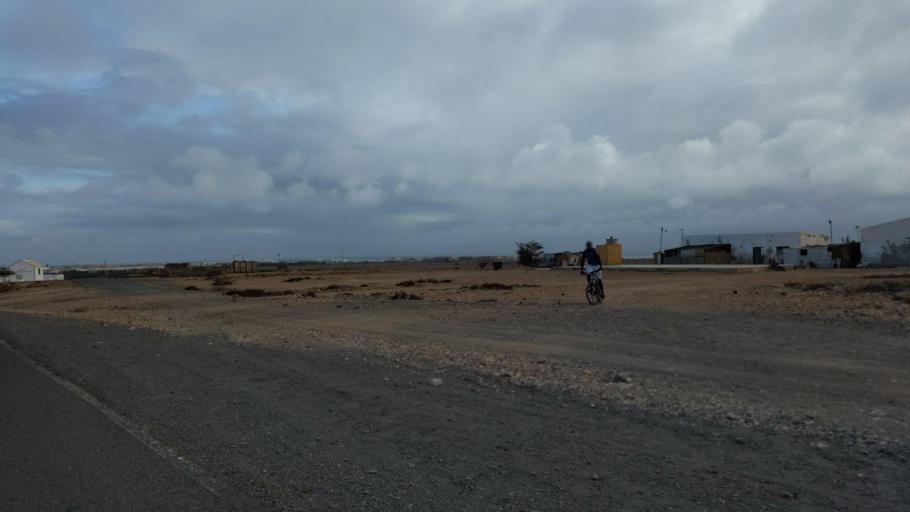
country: CV
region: Sal
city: Santa Maria
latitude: 16.6345
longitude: -22.9175
